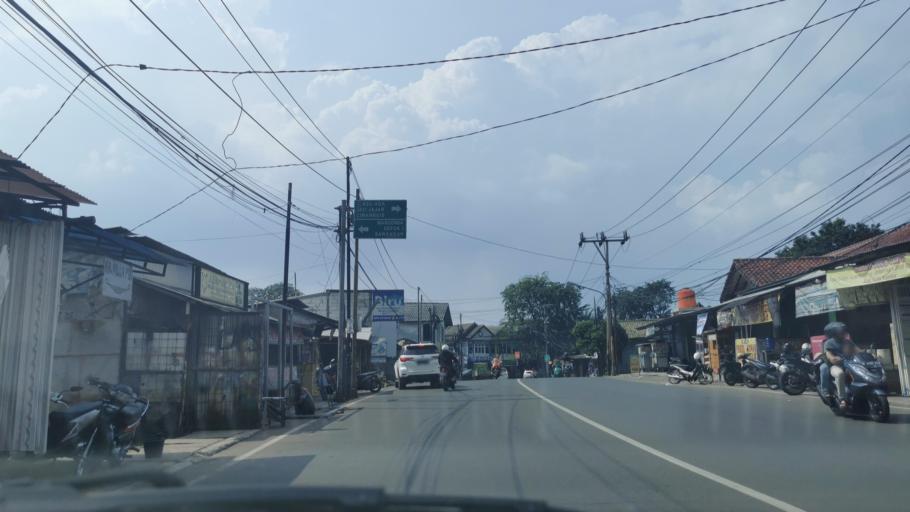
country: ID
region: West Java
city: Depok
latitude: -6.4047
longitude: 106.8378
